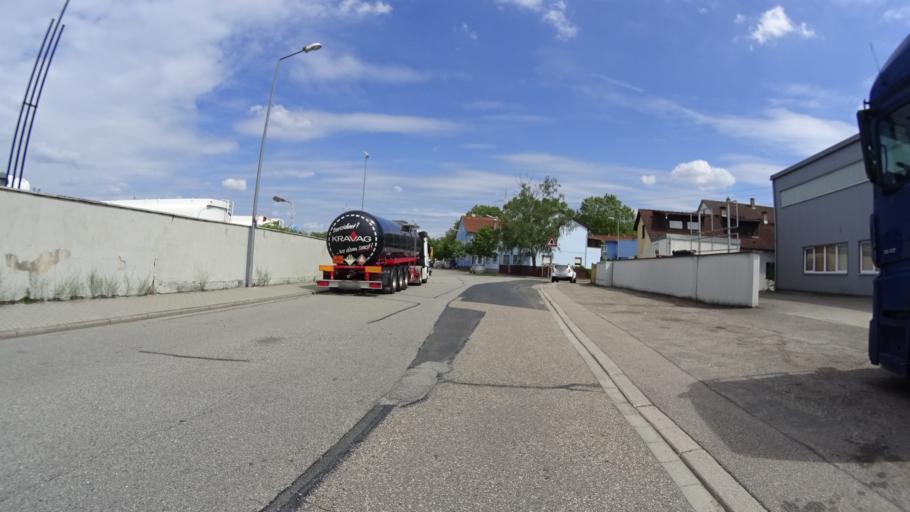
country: DE
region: Baden-Wuerttemberg
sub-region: Karlsruhe Region
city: Rheinstetten
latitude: 49.0095
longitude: 8.3326
